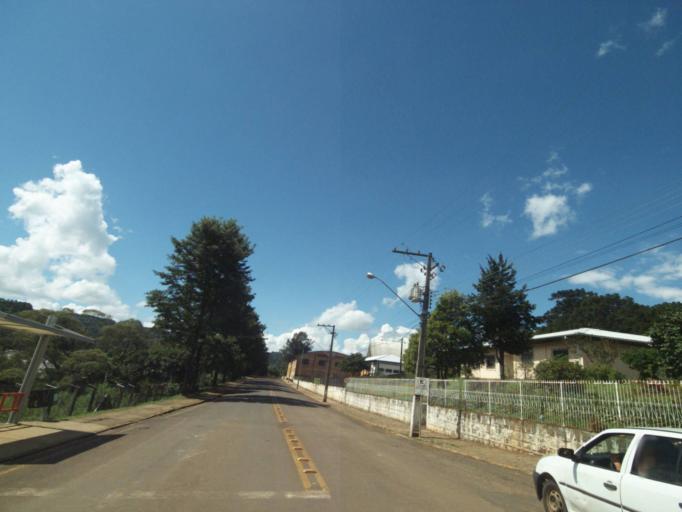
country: BR
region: Parana
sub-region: Uniao Da Vitoria
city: Uniao da Vitoria
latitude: -26.1646
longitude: -51.5532
